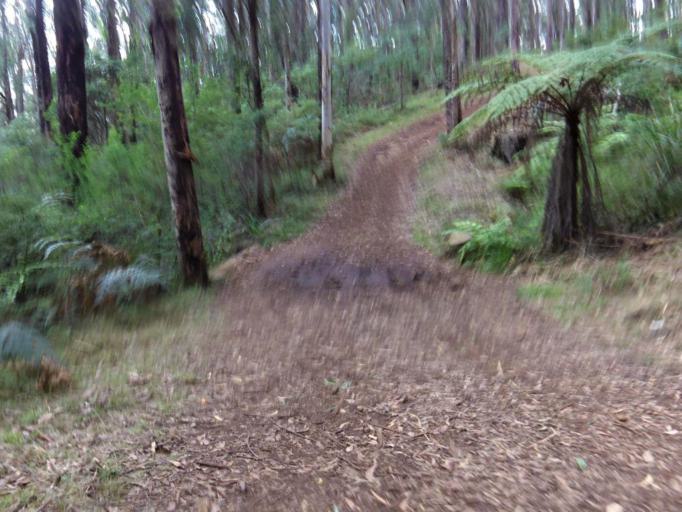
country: AU
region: Victoria
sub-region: Yarra Ranges
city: Ferny Creek
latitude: -37.8718
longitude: 145.3229
